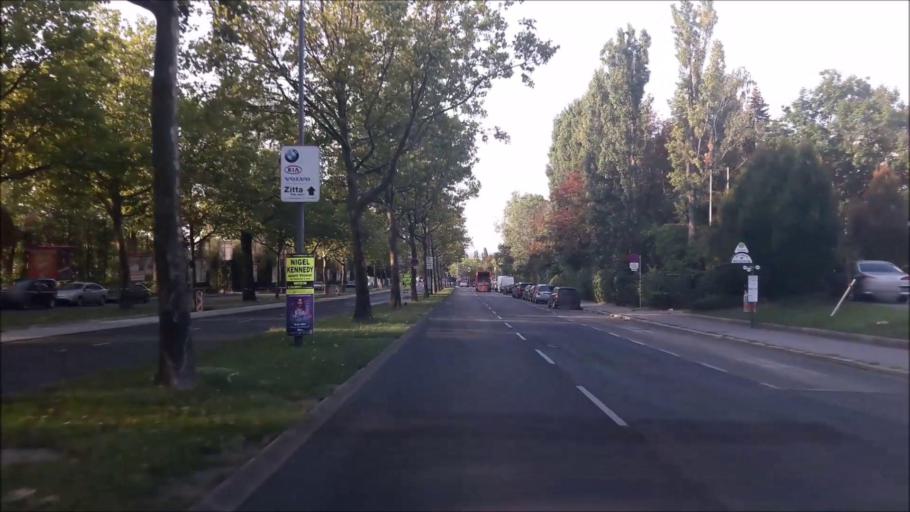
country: AT
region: Vienna
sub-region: Wien Stadt
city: Vienna
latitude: 48.1611
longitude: 16.3669
